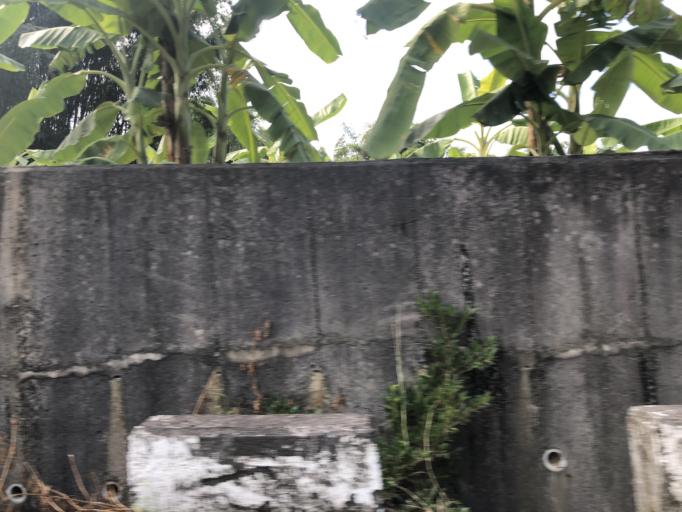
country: TW
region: Taiwan
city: Yujing
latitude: 23.0386
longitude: 120.4210
